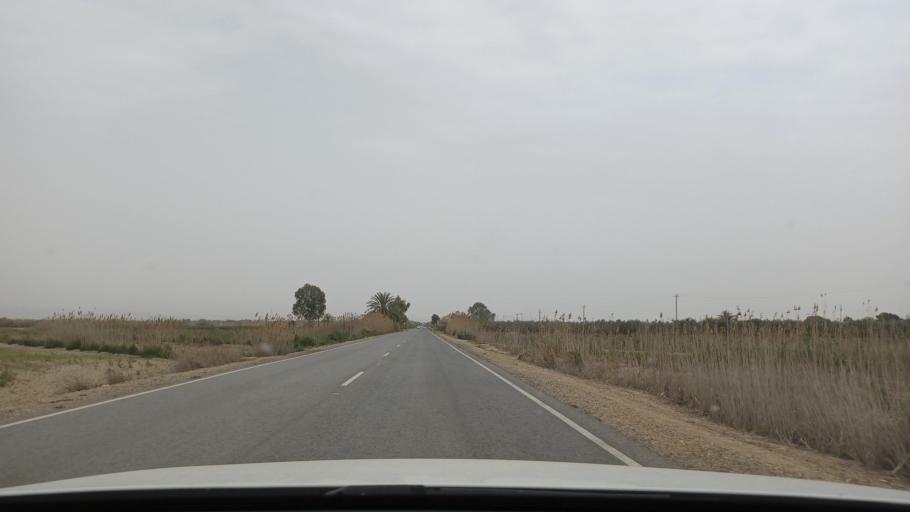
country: ES
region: Valencia
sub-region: Provincia de Alicante
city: Daya Vieja
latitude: 38.1632
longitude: -0.7029
